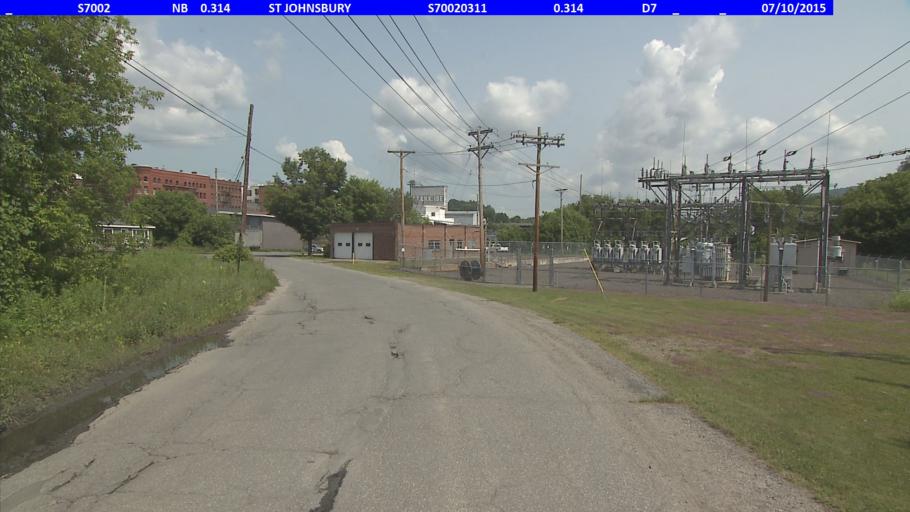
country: US
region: Vermont
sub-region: Caledonia County
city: Saint Johnsbury
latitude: 44.4164
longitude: -72.0141
